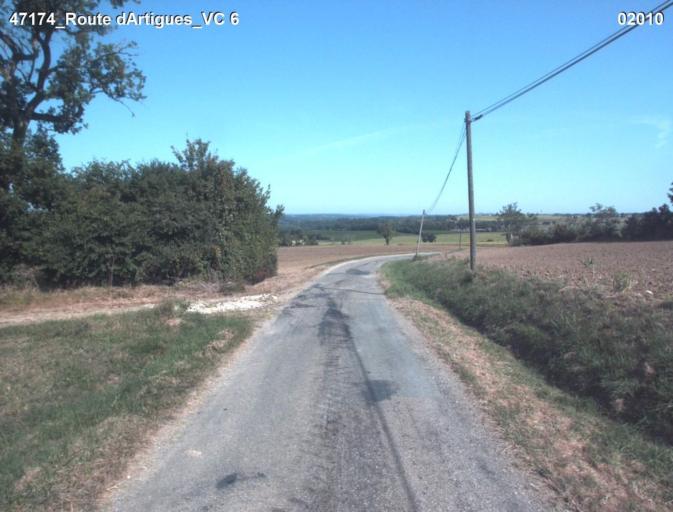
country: FR
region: Midi-Pyrenees
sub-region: Departement du Gers
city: Condom
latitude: 44.0247
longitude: 0.3332
